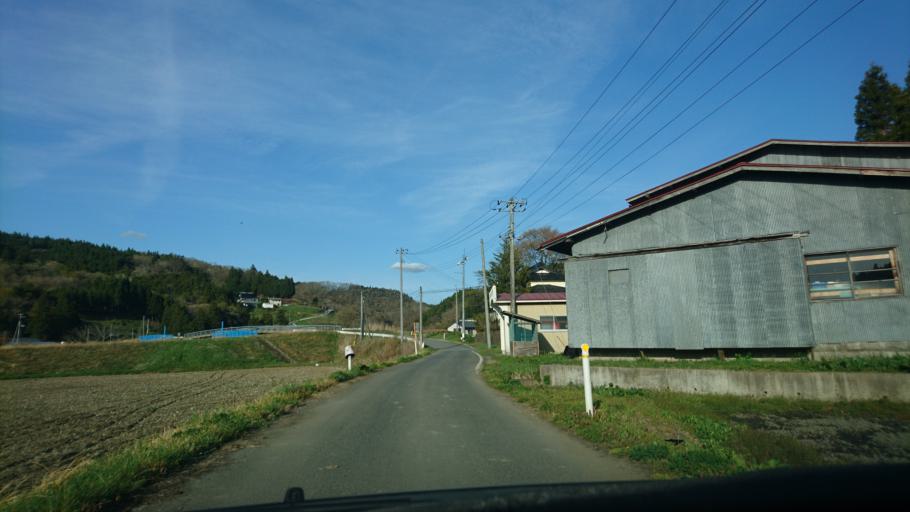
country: JP
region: Iwate
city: Ichinoseki
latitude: 38.8956
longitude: 141.2993
